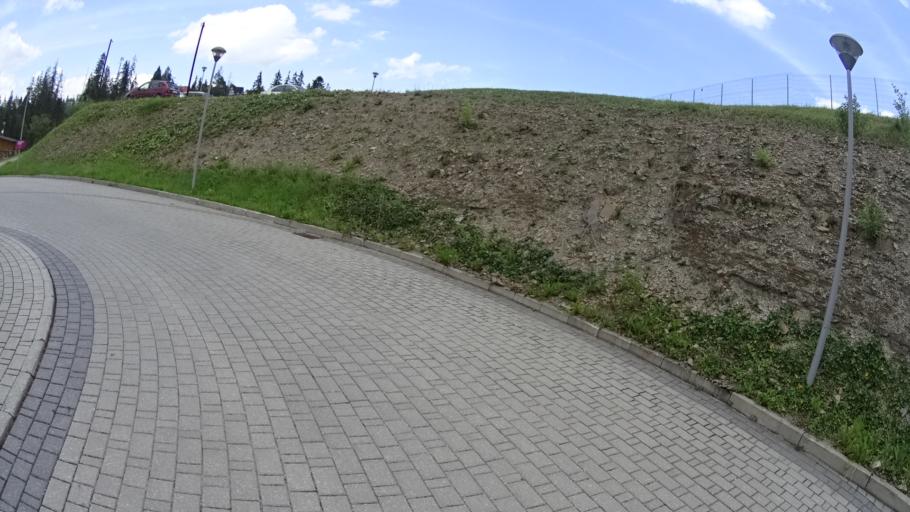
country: PL
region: Lesser Poland Voivodeship
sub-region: Powiat tatrzanski
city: Bukowina Tatrzanska
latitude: 49.3267
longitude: 20.0942
